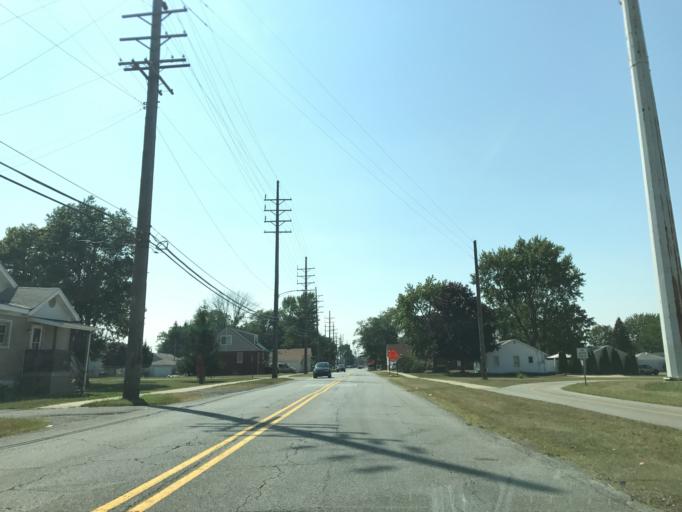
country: US
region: Illinois
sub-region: Cook County
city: Calumet City
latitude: 41.6321
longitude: -87.5039
